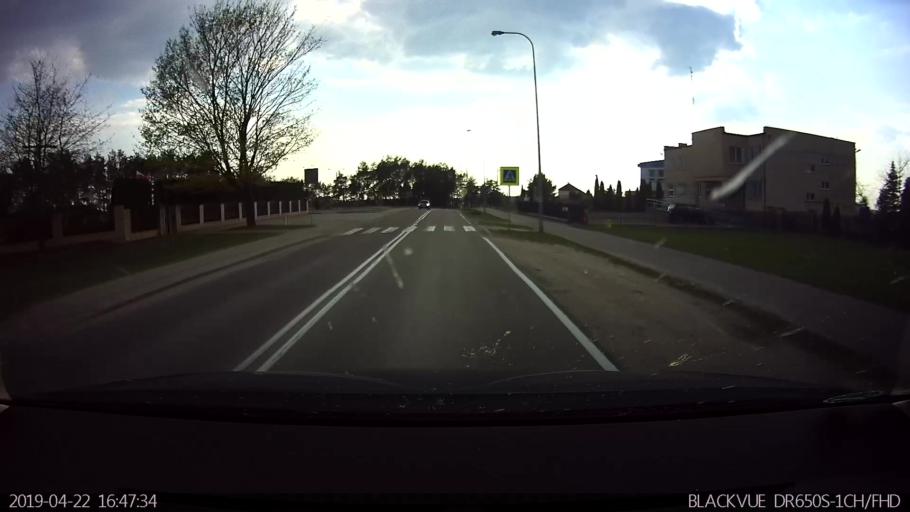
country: PL
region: Podlasie
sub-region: Powiat siemiatycki
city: Siemiatycze
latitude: 52.4314
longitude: 22.8844
